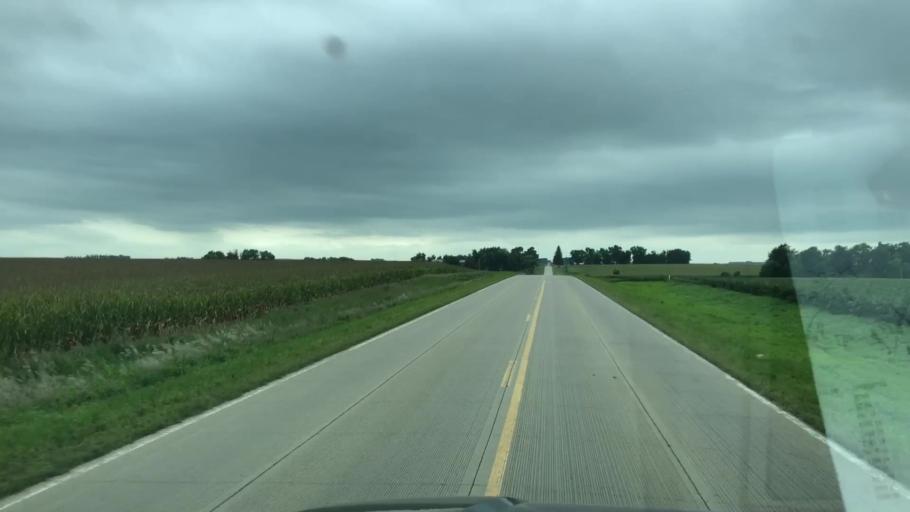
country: US
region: Iowa
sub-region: Sioux County
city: Alton
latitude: 43.1168
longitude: -95.9788
